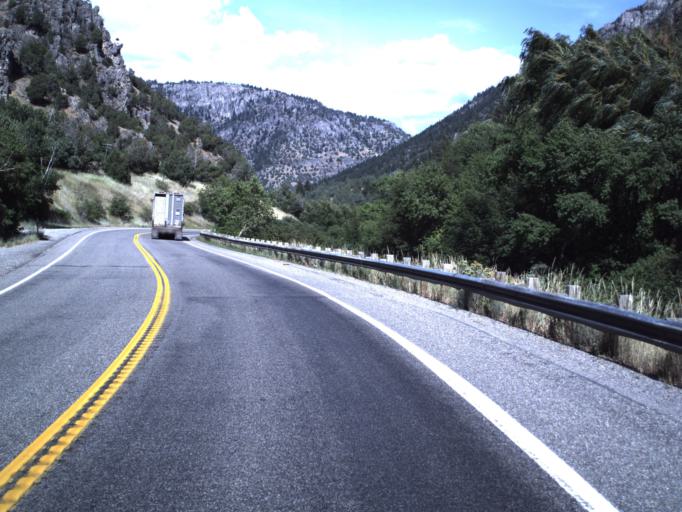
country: US
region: Utah
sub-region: Cache County
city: North Logan
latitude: 41.7676
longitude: -111.6640
